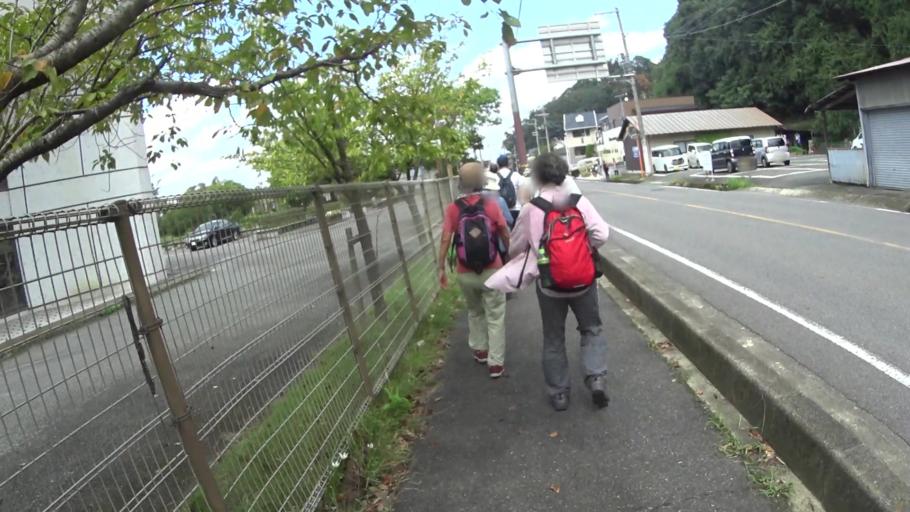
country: JP
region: Nara
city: Sakurai
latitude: 34.5027
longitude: 135.8530
